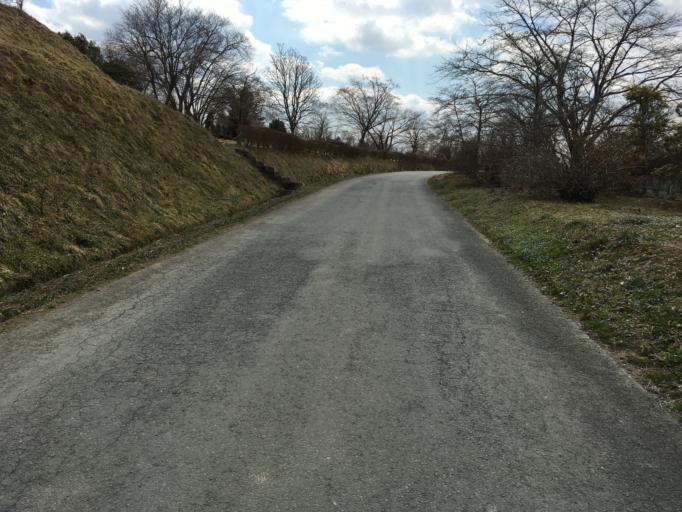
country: JP
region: Iwate
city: Ichinoseki
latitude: 38.8184
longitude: 141.2719
